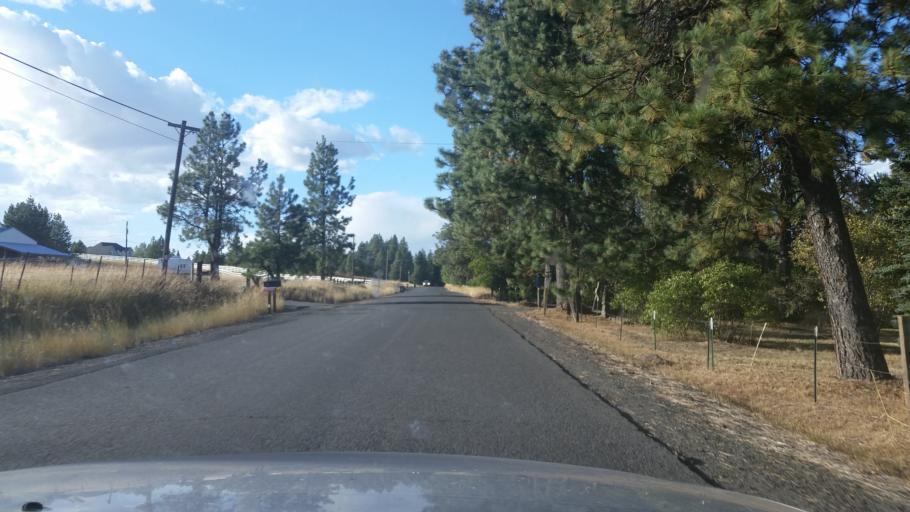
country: US
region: Washington
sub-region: Spokane County
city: Cheney
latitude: 47.5225
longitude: -117.5757
